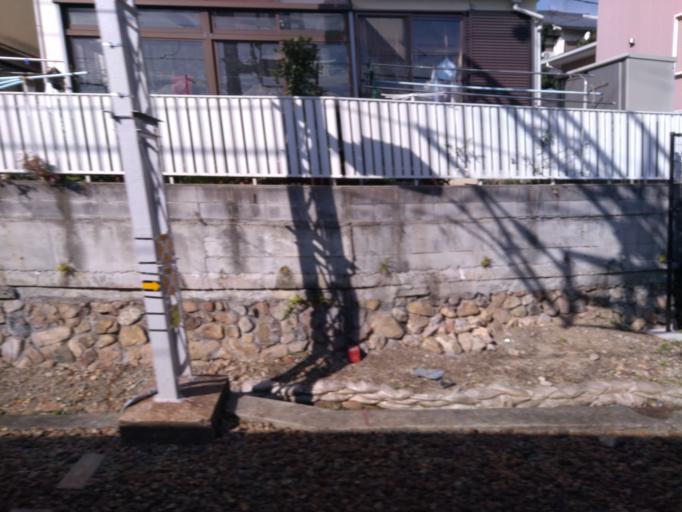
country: JP
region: Hyogo
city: Takarazuka
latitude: 34.8114
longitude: 135.3566
